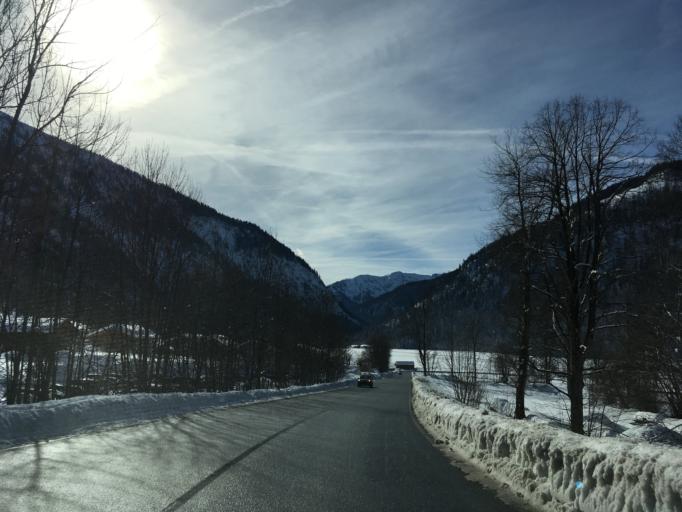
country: DE
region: Bavaria
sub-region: Upper Bavaria
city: Bayrischzell
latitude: 47.6750
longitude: 12.0212
